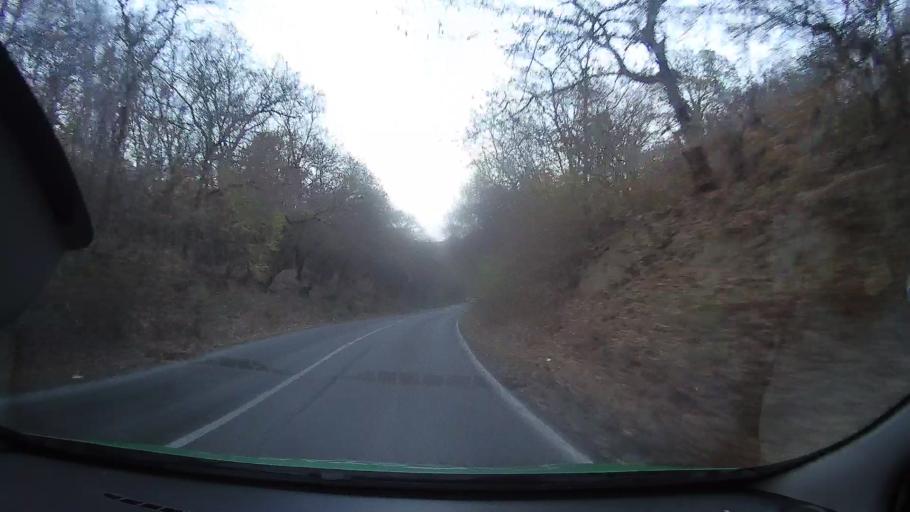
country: RO
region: Constanta
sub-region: Comuna Baneasa
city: Baneasa
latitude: 44.0915
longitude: 27.6535
